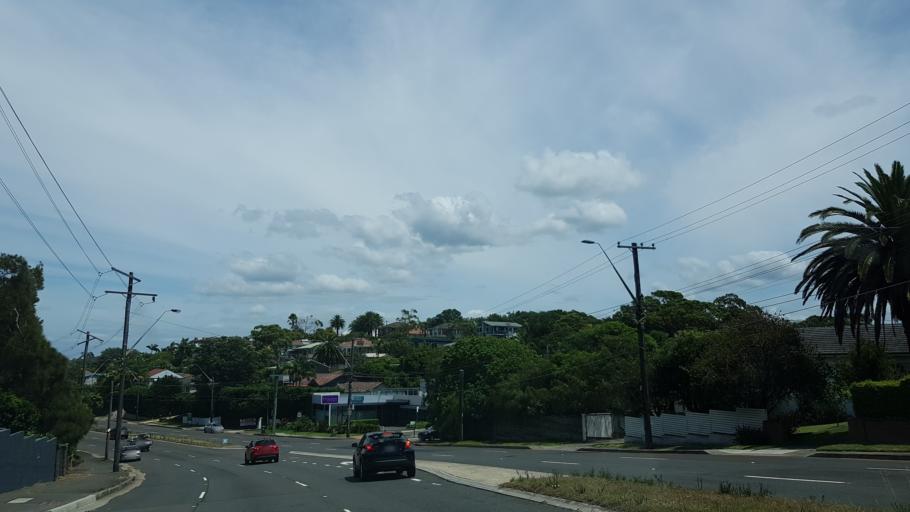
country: AU
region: New South Wales
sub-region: Pittwater
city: Newport
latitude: -33.6705
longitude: 151.3141
